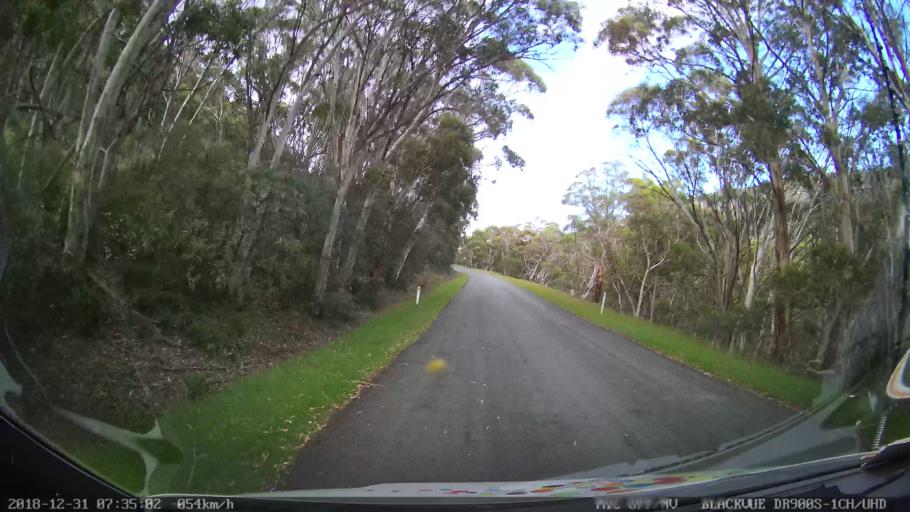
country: AU
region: New South Wales
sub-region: Snowy River
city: Jindabyne
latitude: -36.3326
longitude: 148.4470
